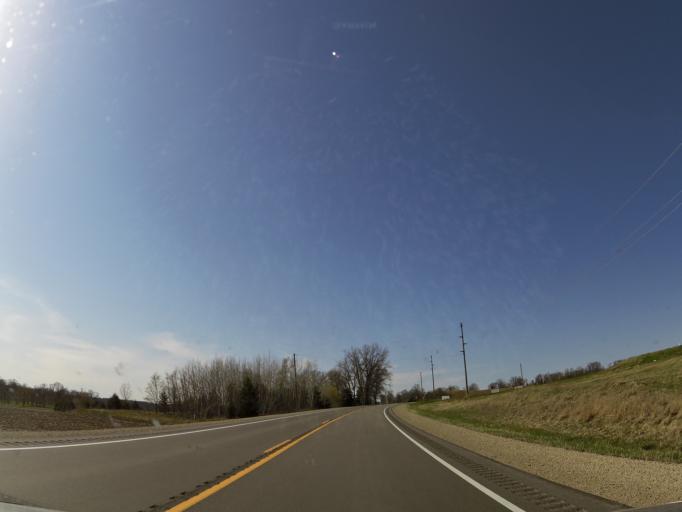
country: US
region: Wisconsin
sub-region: Pierce County
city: Ellsworth
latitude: 44.7168
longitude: -92.4320
